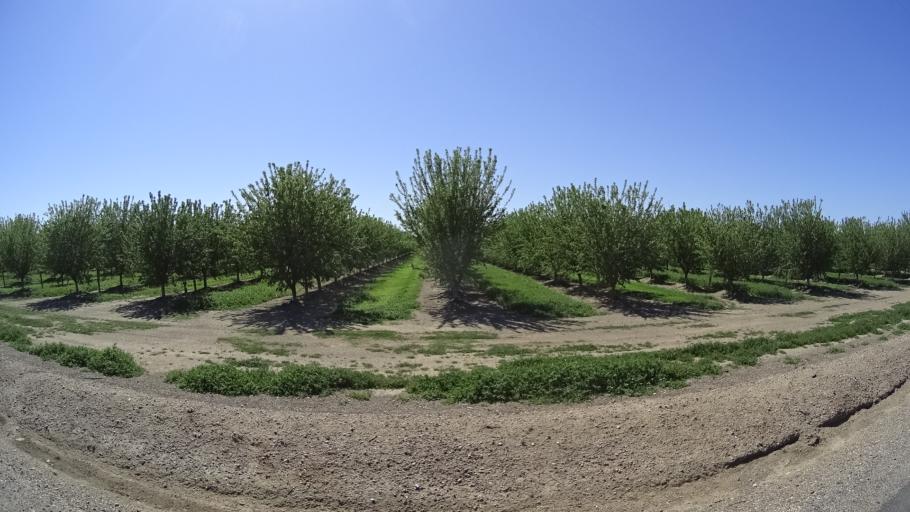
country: US
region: California
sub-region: Glenn County
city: Orland
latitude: 39.6972
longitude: -122.2438
